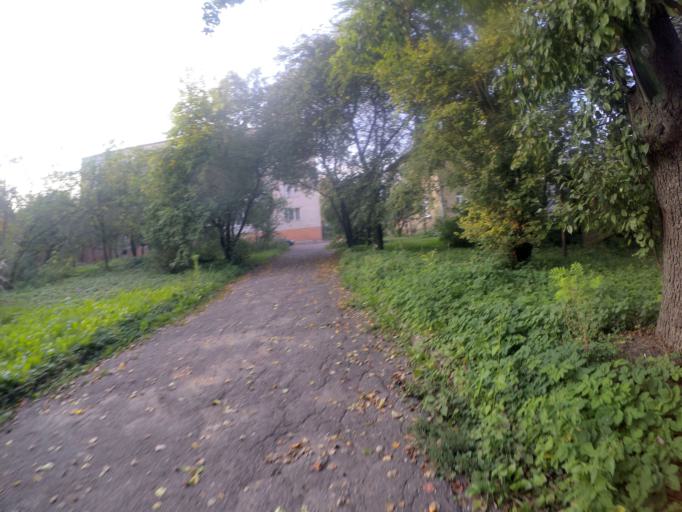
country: BY
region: Grodnenskaya
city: Hrodna
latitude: 53.6874
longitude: 23.8331
